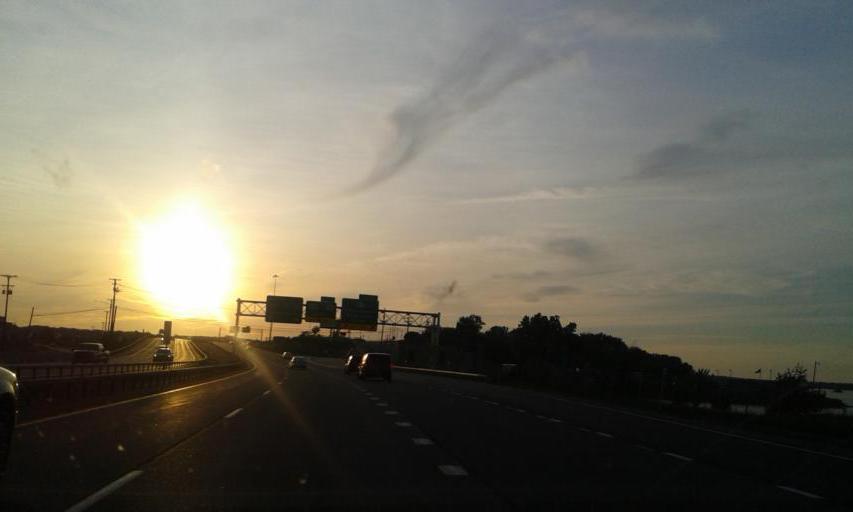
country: US
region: New York
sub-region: Onondaga County
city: Solvay
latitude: 43.0704
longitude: -76.2028
